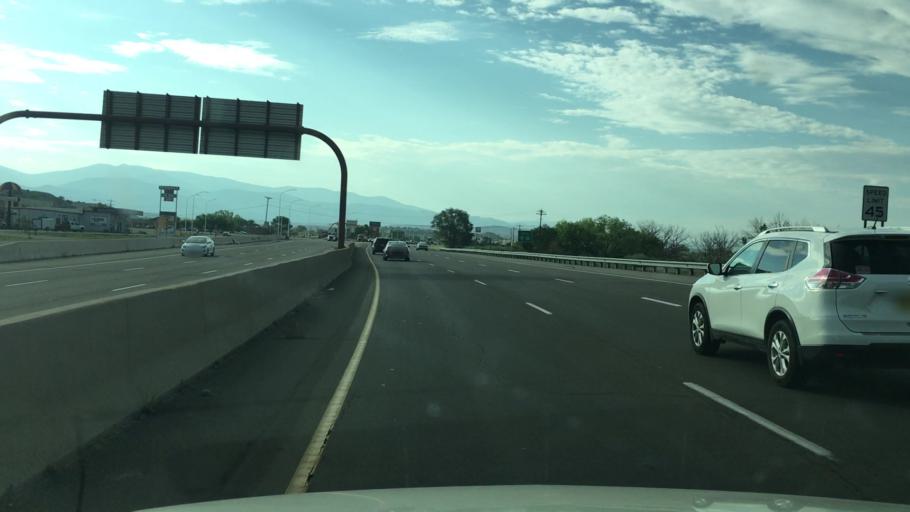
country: US
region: New Mexico
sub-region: Santa Fe County
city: Pojoaque
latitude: 35.8875
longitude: -106.0205
